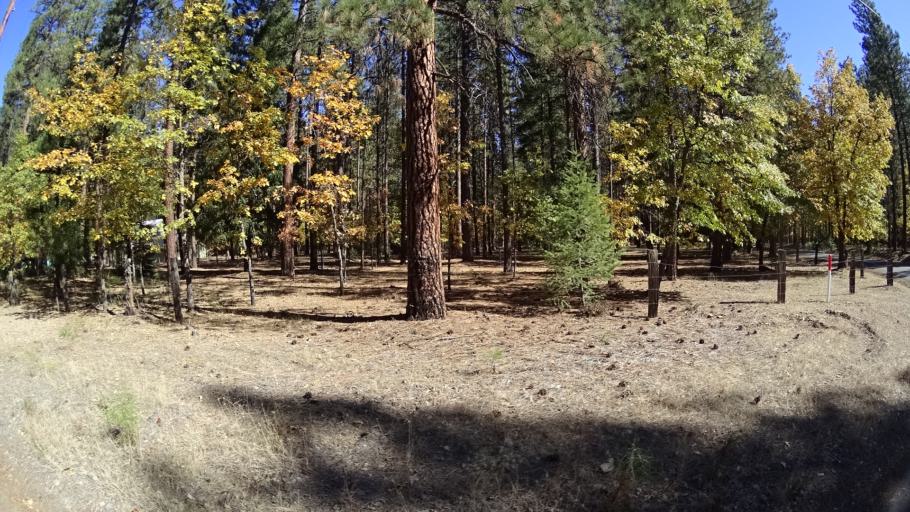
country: US
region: California
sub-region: Siskiyou County
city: Yreka
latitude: 41.5818
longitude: -122.9746
